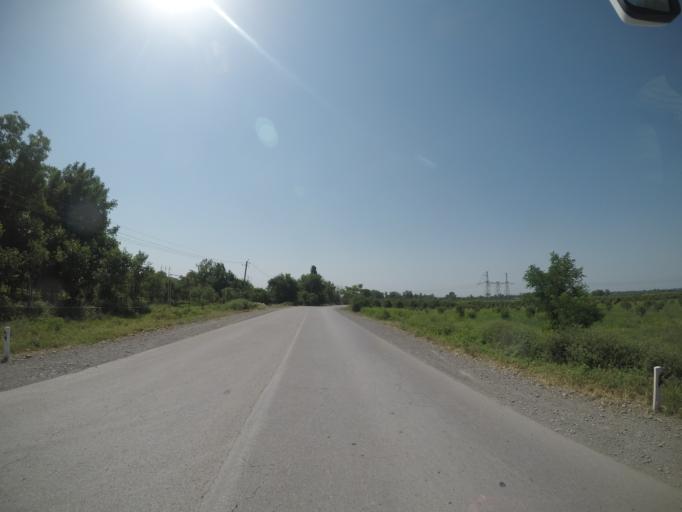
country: AZ
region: Agdas
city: Agdas
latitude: 40.7041
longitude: 47.5403
